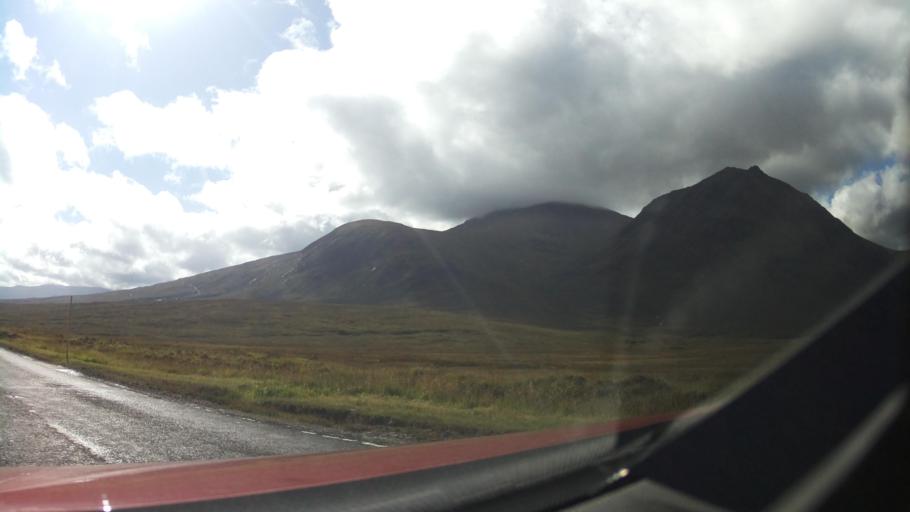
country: GB
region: Scotland
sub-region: Highland
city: Spean Bridge
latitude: 56.6560
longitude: -4.8667
